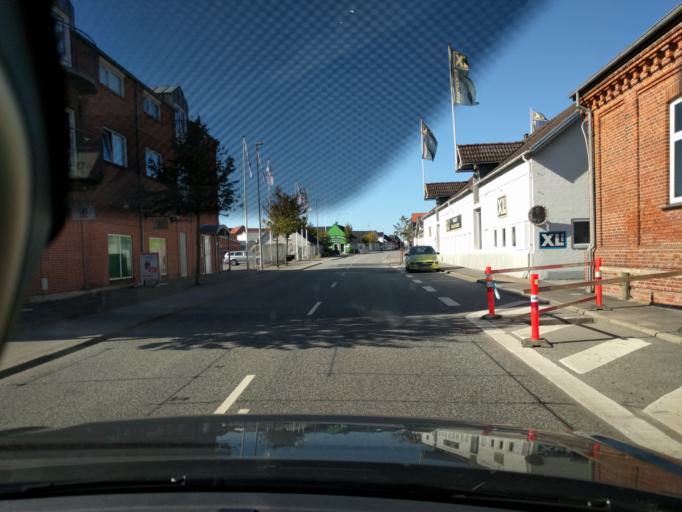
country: DK
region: North Denmark
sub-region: Vesthimmerland Kommune
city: Alestrup
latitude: 56.7065
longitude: 9.6318
